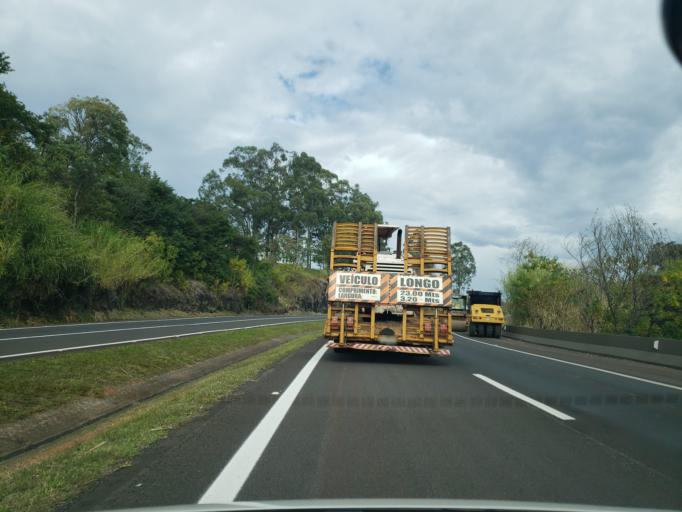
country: BR
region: Sao Paulo
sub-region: Dois Corregos
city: Dois Corregos
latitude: -22.2481
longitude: -48.3532
